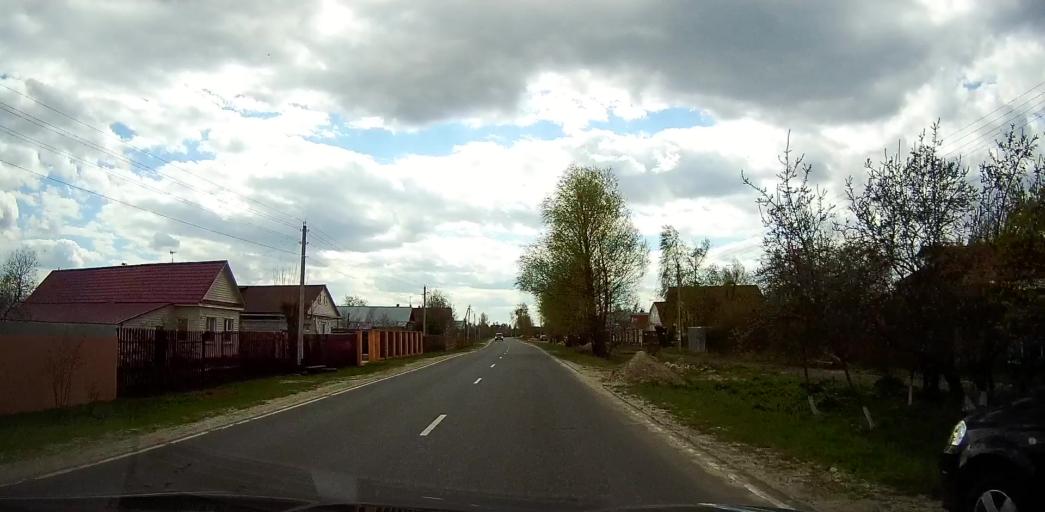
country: RU
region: Moskovskaya
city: Drezna
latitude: 55.6668
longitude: 38.7615
